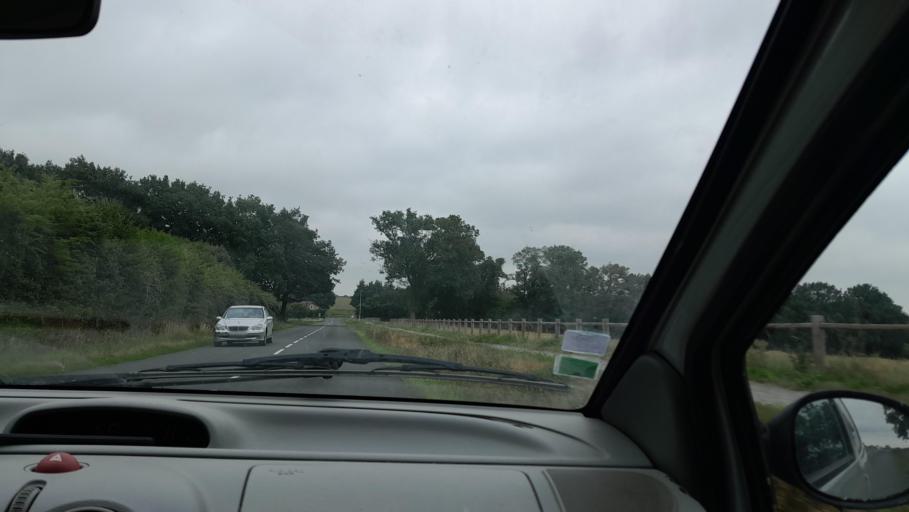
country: FR
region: Pays de la Loire
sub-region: Departement de la Mayenne
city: Cosse-le-Vivien
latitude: 47.9378
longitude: -0.9003
